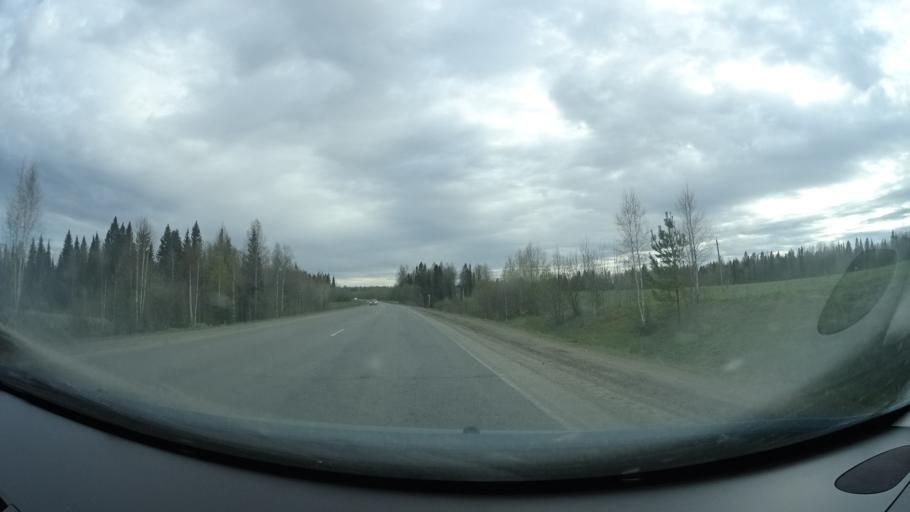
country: RU
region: Perm
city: Yugo-Kamskiy
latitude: 57.7719
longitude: 55.7511
